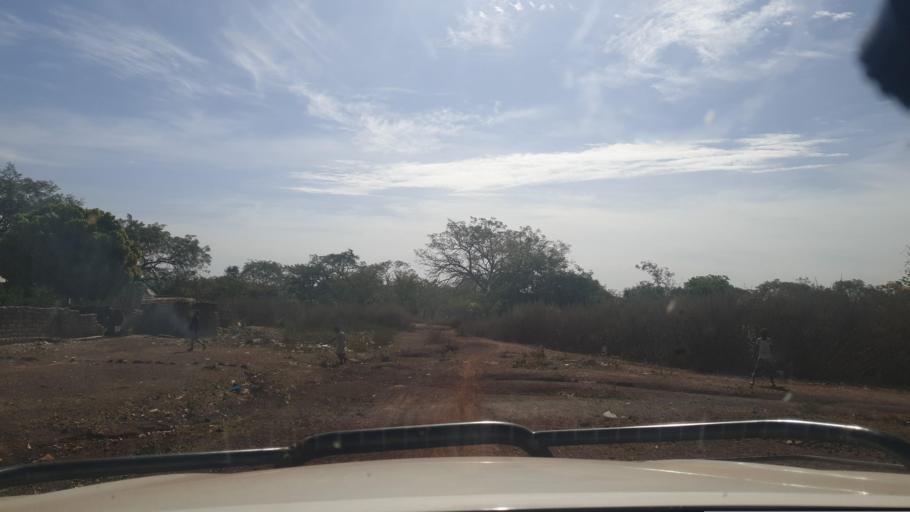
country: GN
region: Kankan
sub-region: Mandiana Prefecture
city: Mandiana
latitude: 10.4876
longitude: -8.0957
